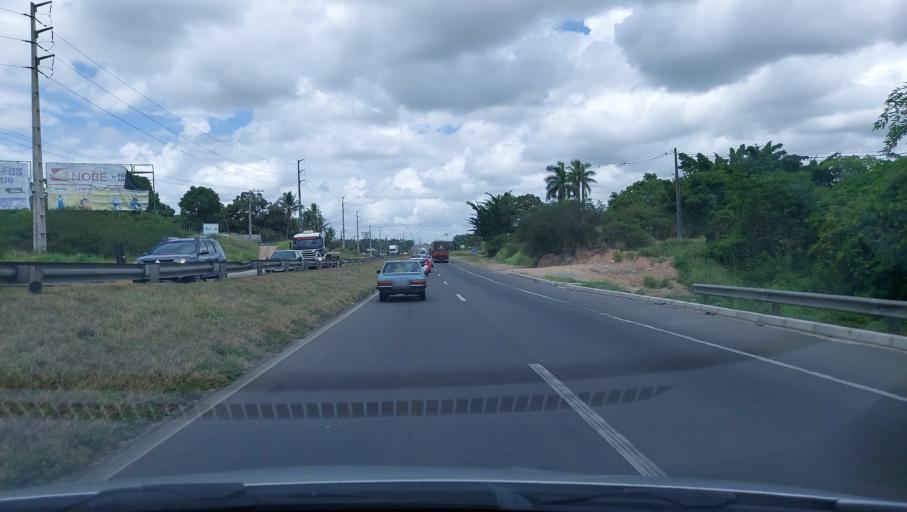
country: BR
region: Bahia
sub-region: Conceicao Do Jacuipe
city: Conceicao do Jacuipe
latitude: -12.3272
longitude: -38.8628
